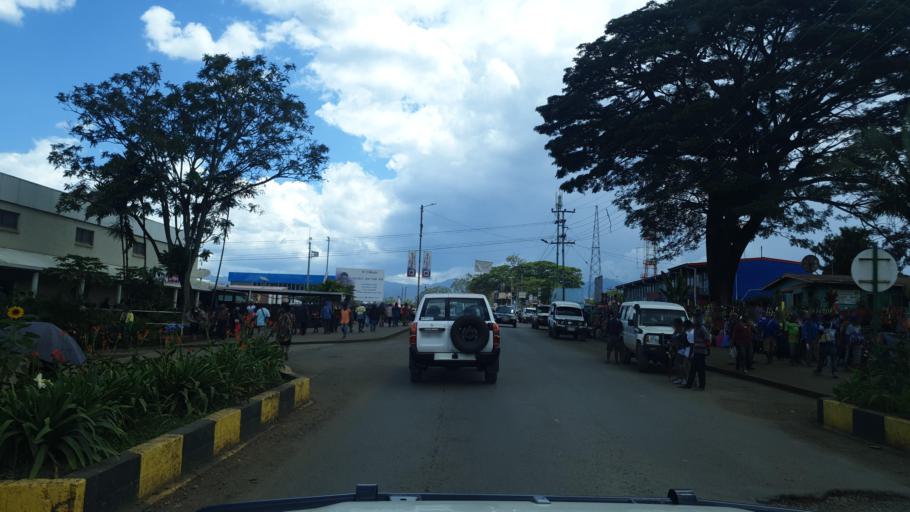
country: PG
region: Eastern Highlands
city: Goroka
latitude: -6.0730
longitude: 145.3939
